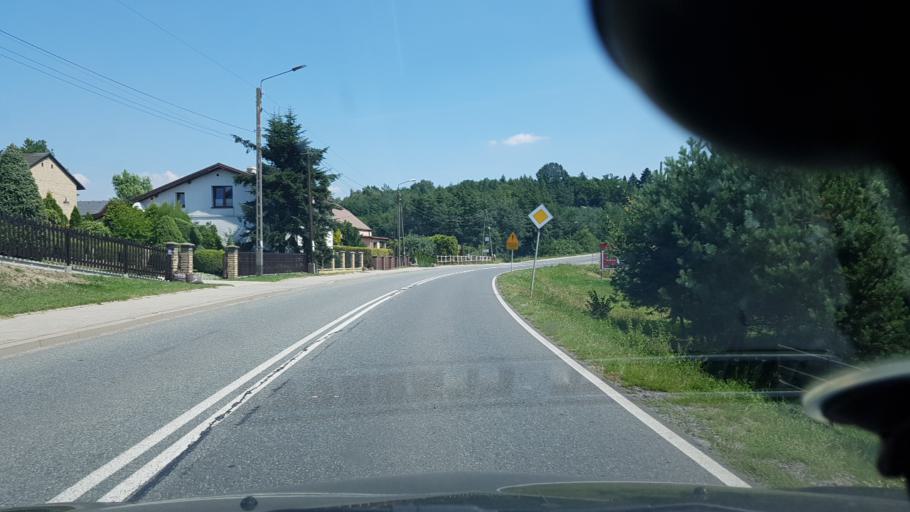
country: PL
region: Silesian Voivodeship
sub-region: Powiat wodzislawski
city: Marklowice
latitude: 50.0173
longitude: 18.5230
